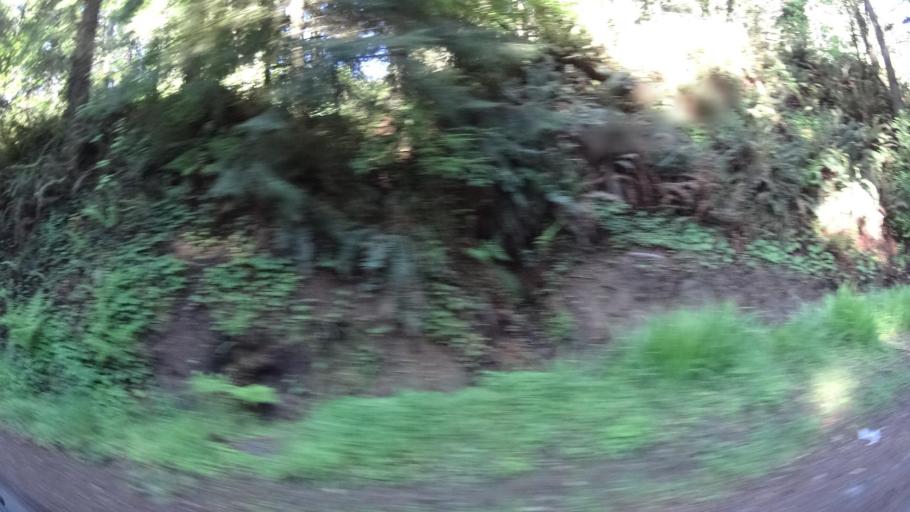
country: US
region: California
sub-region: Humboldt County
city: McKinleyville
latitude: 40.9822
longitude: -124.0985
